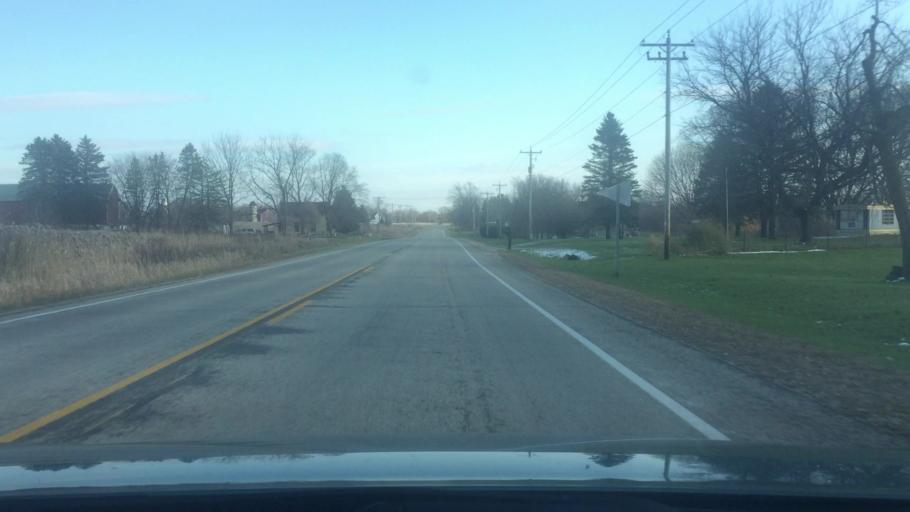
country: US
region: Wisconsin
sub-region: Walworth County
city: Whitewater
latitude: 42.9342
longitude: -88.7283
